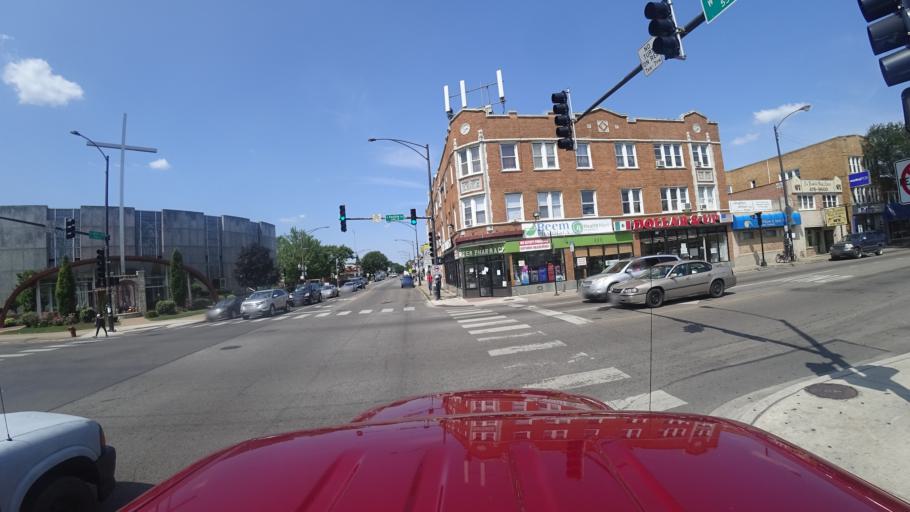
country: US
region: Illinois
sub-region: Cook County
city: Hometown
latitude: 41.7936
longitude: -87.7034
